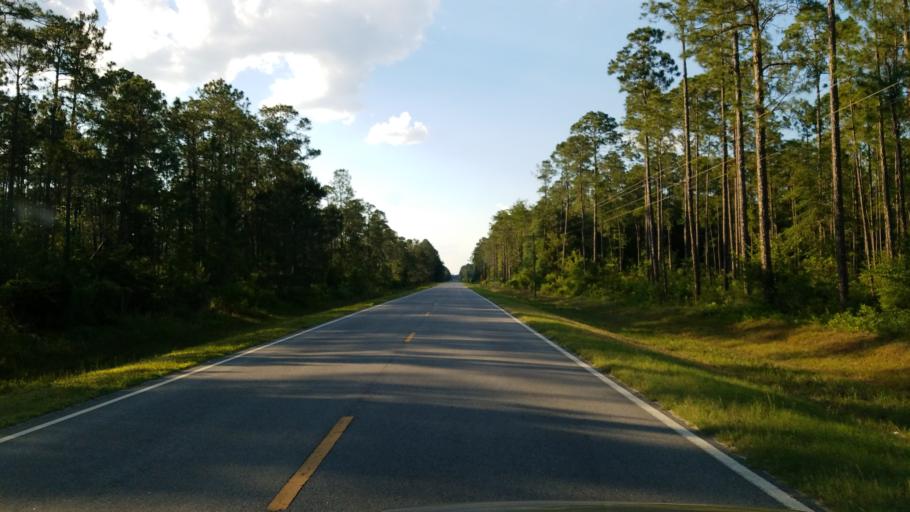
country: US
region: Georgia
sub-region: Lanier County
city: Lakeland
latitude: 31.1048
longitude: -83.0803
